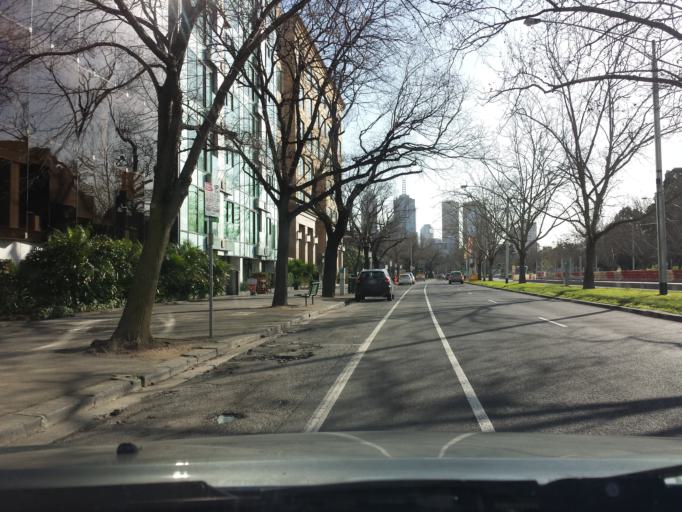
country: AU
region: Victoria
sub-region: Port Phillip
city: South Melbourne
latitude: -37.8298
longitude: 144.9710
